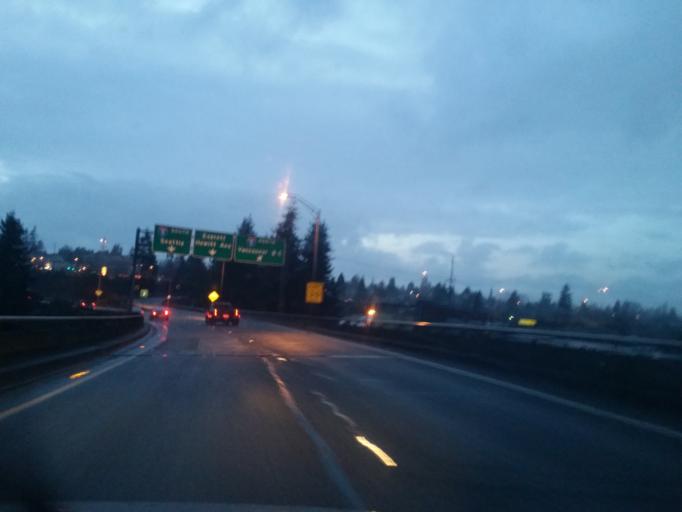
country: US
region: Washington
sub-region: Snohomish County
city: Everett
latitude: 47.9802
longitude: -122.1829
